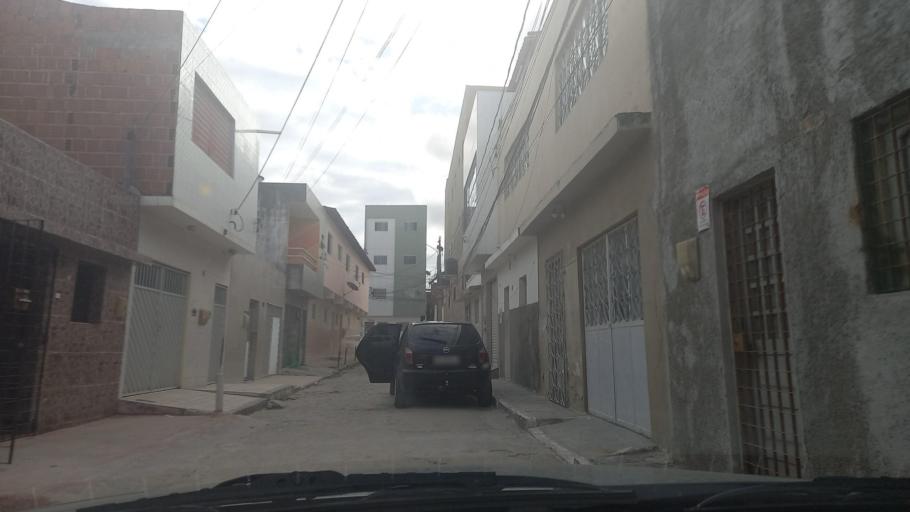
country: BR
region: Pernambuco
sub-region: Caruaru
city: Caruaru
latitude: -8.2918
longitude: -35.9767
